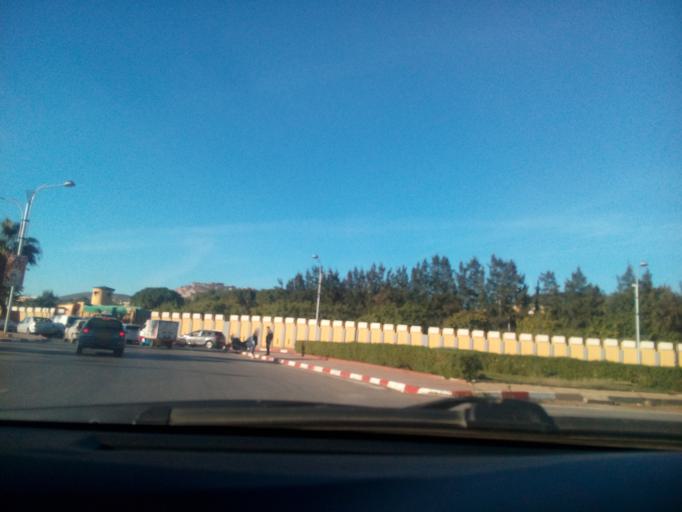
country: DZ
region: Oran
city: Oran
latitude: 35.6844
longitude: -0.6702
